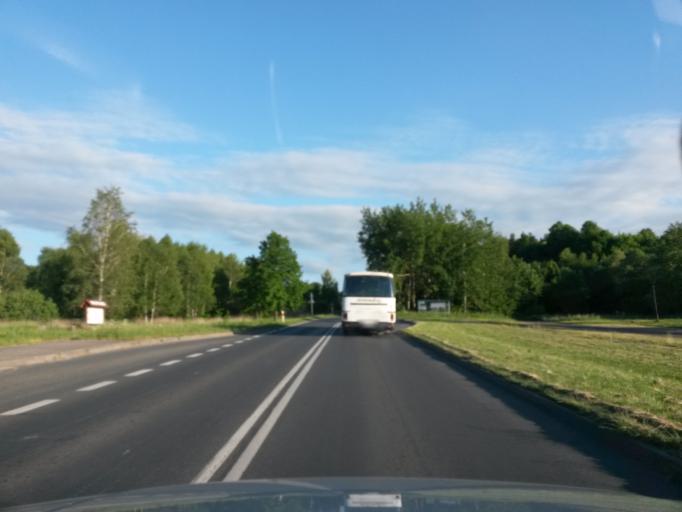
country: PL
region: Lower Silesian Voivodeship
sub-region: Jelenia Gora
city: Jelenia Gora
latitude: 50.8813
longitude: 15.7588
